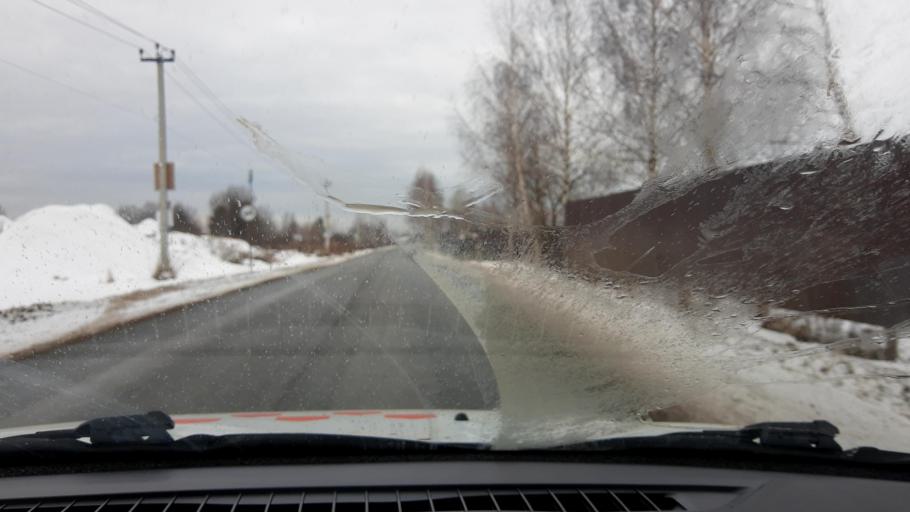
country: RU
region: Nizjnij Novgorod
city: Neklyudovo
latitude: 56.4245
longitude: 43.9626
